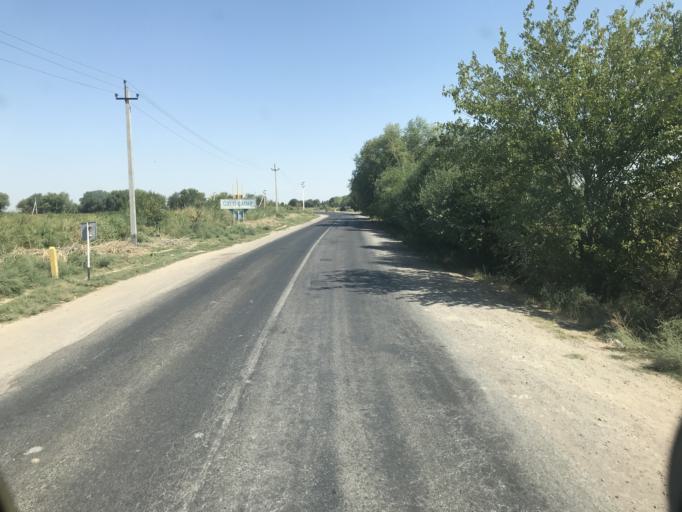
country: KZ
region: Ongtustik Qazaqstan
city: Ilyich
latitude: 40.9462
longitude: 68.4886
